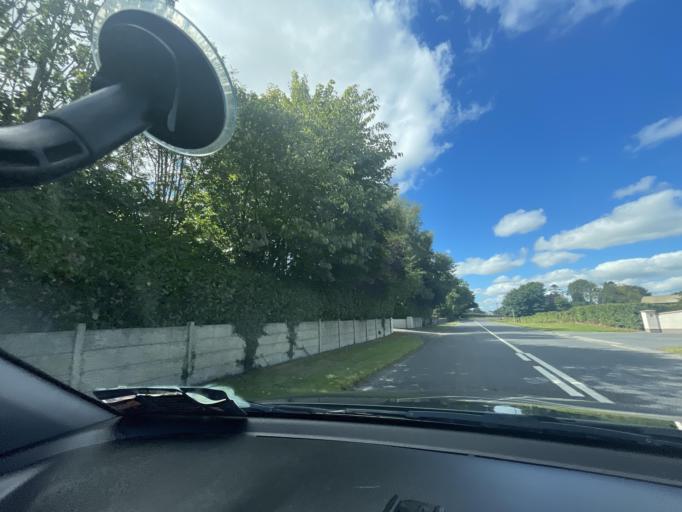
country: IE
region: Leinster
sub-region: An Mhi
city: Dunshaughlin
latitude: 53.5183
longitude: -6.6391
